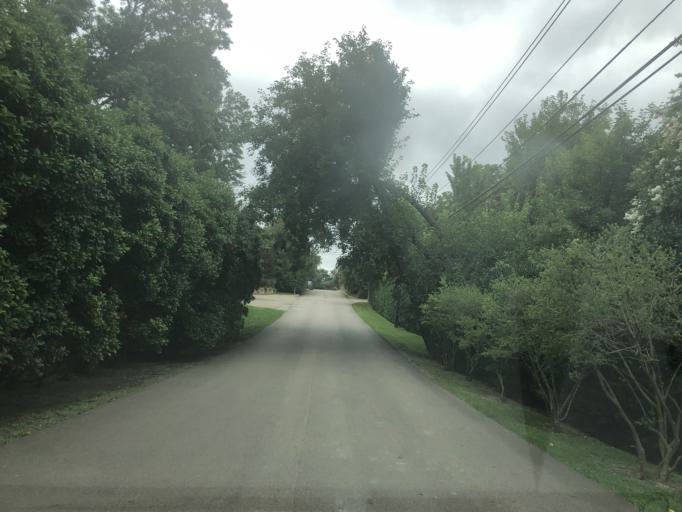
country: US
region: Texas
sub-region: Dallas County
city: University Park
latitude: 32.8682
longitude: -96.8141
